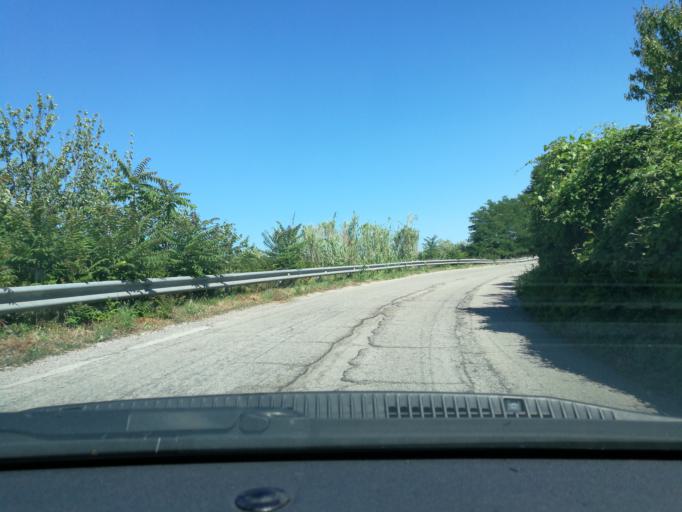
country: IT
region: Abruzzo
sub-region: Provincia di Chieti
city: Vasto
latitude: 42.1655
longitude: 14.7021
